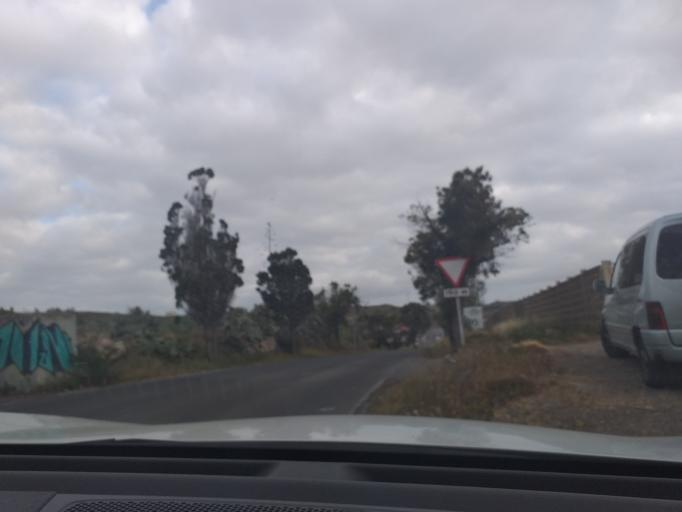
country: ES
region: Canary Islands
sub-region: Provincia de Las Palmas
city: Arucas
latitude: 28.1053
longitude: -15.4886
